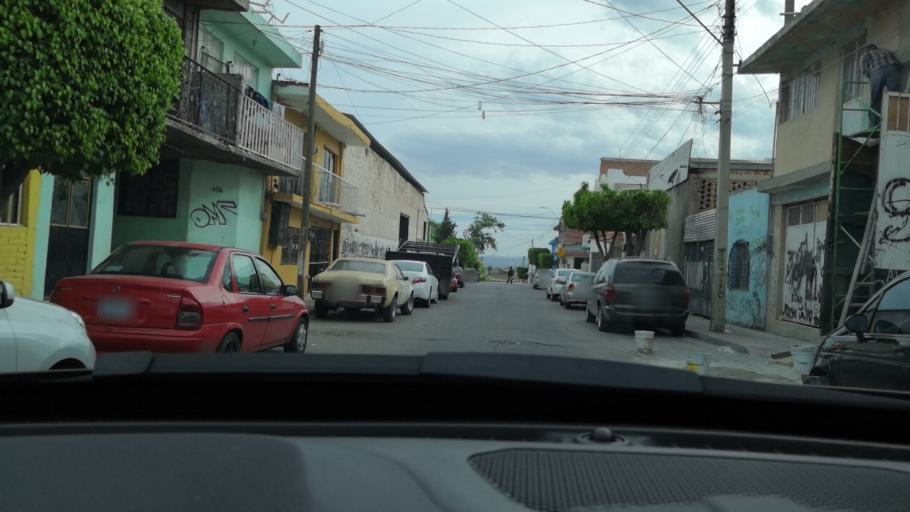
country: MX
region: Guanajuato
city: Leon
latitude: 21.1284
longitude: -101.7063
